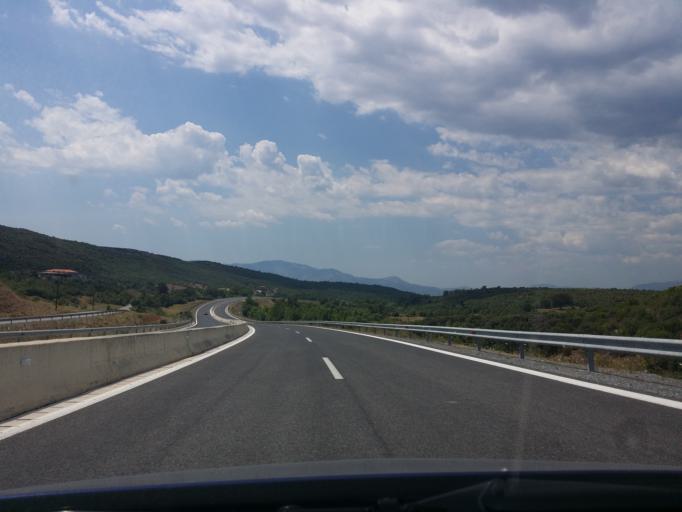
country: GR
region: Peloponnese
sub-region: Nomos Arkadias
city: Megalopoli
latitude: 37.3293
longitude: 22.1615
